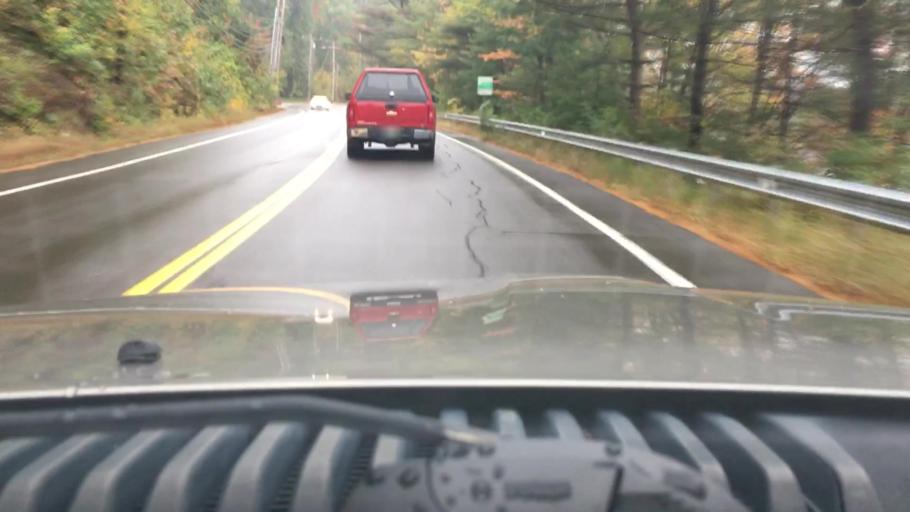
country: US
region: New Hampshire
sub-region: Hillsborough County
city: Manchester
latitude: 43.0224
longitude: -71.4814
